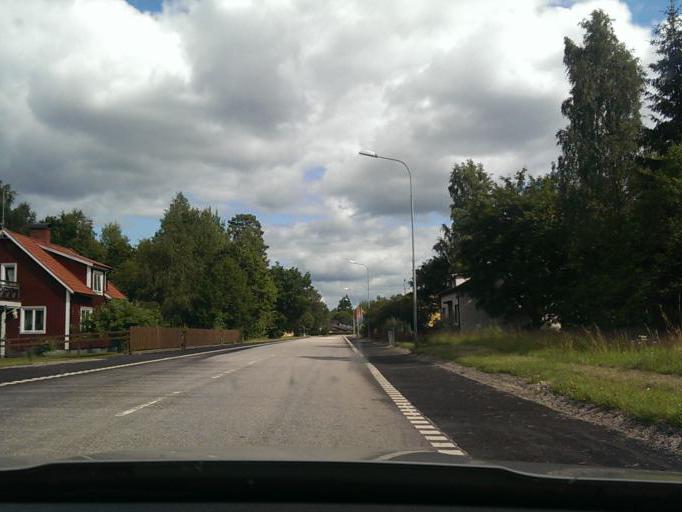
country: SE
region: Kronoberg
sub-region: Ljungby Kommun
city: Lagan
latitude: 56.9720
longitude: 13.9413
